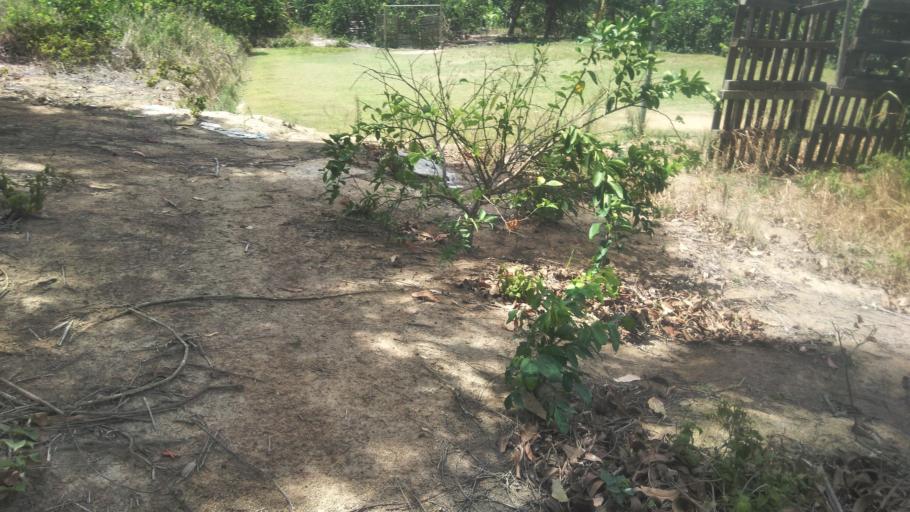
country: BR
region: Pernambuco
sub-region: Vitoria De Santo Antao
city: Vitoria de Santo Antao
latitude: -8.1523
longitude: -35.2484
